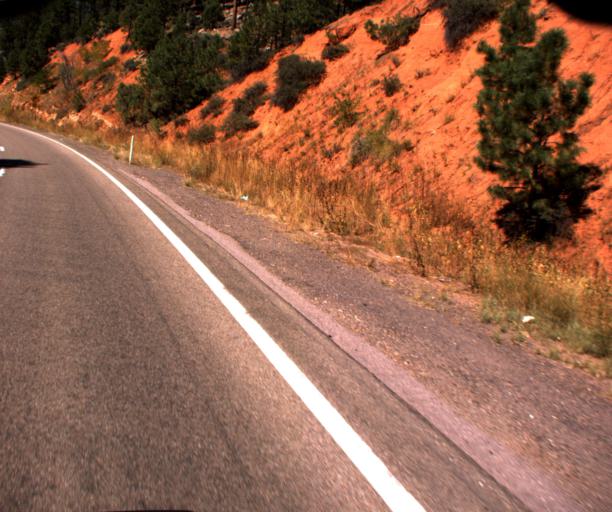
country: US
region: Arizona
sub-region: Gila County
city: Star Valley
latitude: 34.3050
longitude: -110.9223
